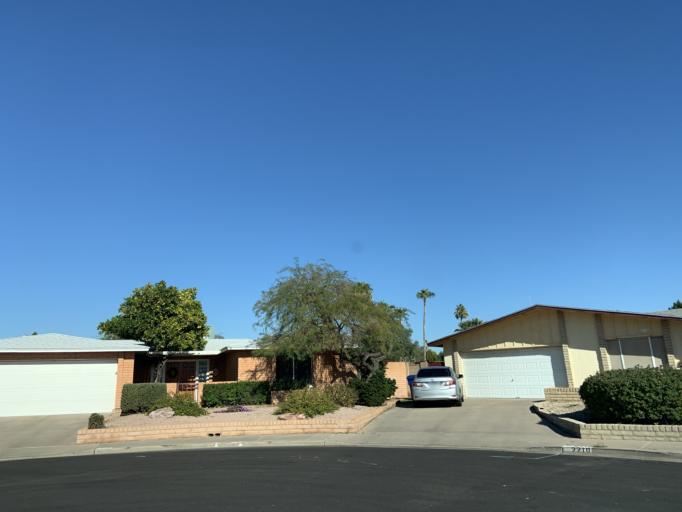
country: US
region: Arizona
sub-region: Maricopa County
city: Tempe
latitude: 33.4019
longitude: -111.8795
